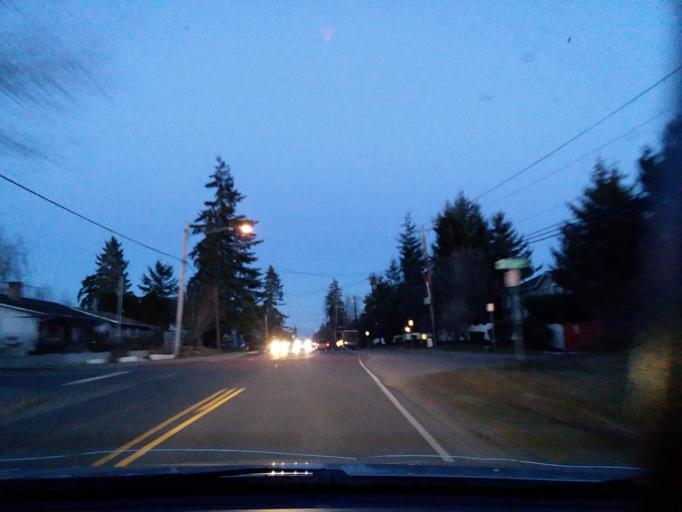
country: US
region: Washington
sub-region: Snohomish County
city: Martha Lake
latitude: 47.9073
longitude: -122.2501
